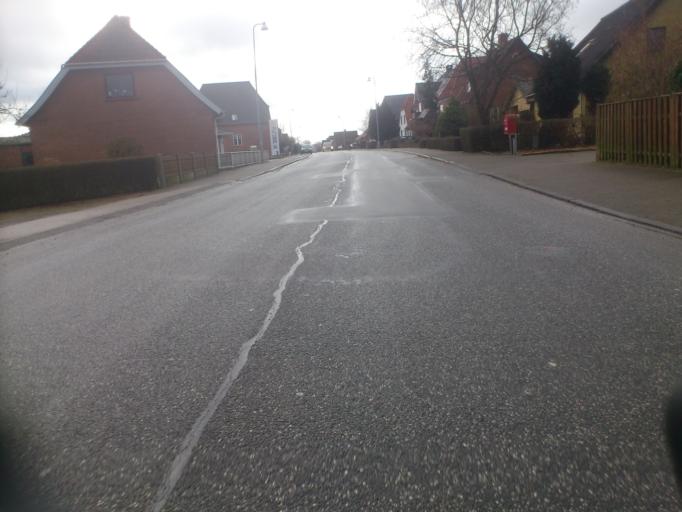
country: DK
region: South Denmark
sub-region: Fredericia Kommune
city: Fredericia
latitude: 55.5763
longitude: 9.7536
